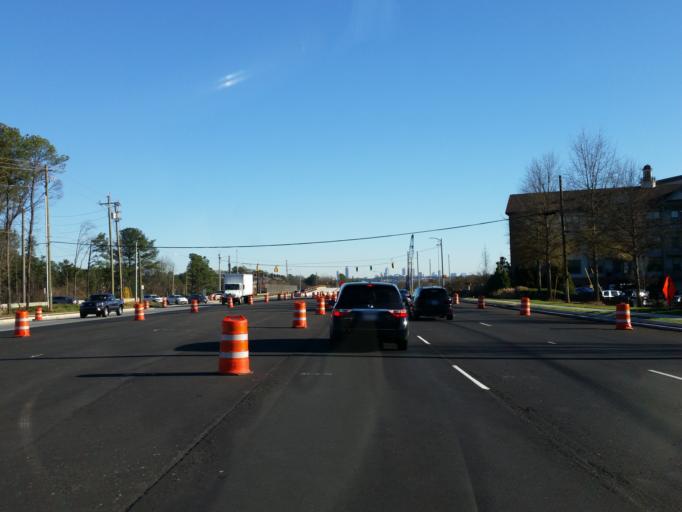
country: US
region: Georgia
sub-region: Cobb County
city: Vinings
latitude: 33.8446
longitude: -84.4897
